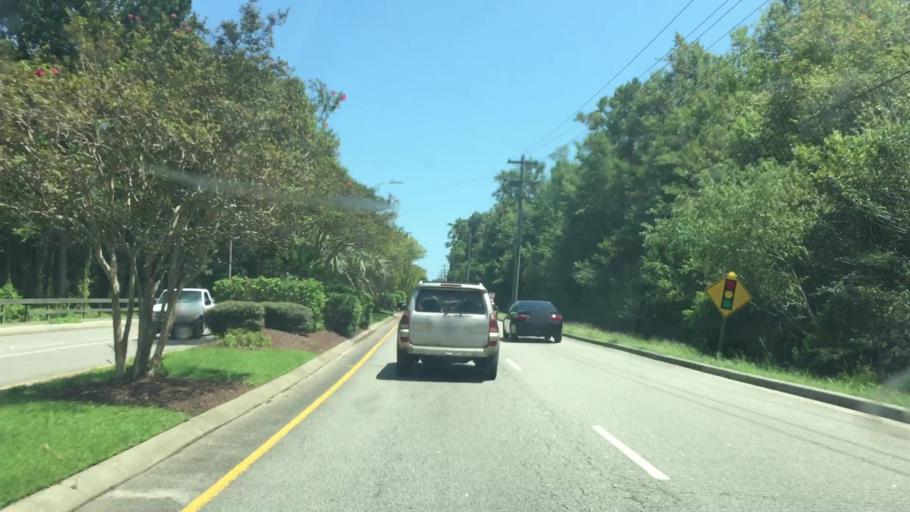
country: US
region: South Carolina
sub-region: Horry County
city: North Myrtle Beach
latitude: 33.8448
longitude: -78.6508
